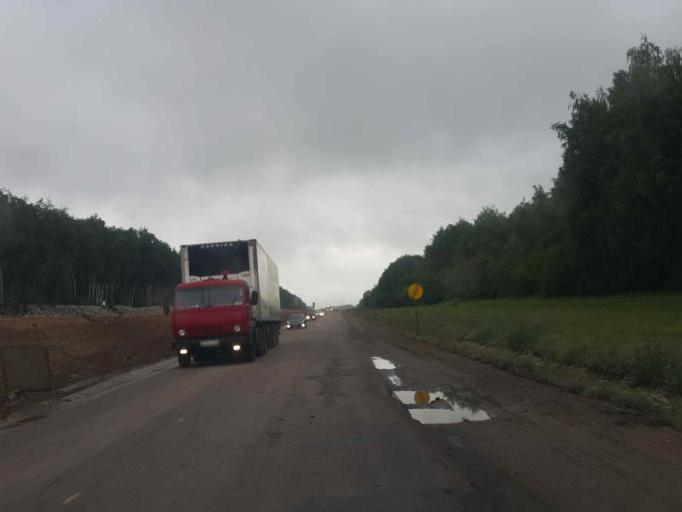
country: RU
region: Tambov
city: Selezni
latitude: 52.7743
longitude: 41.0443
